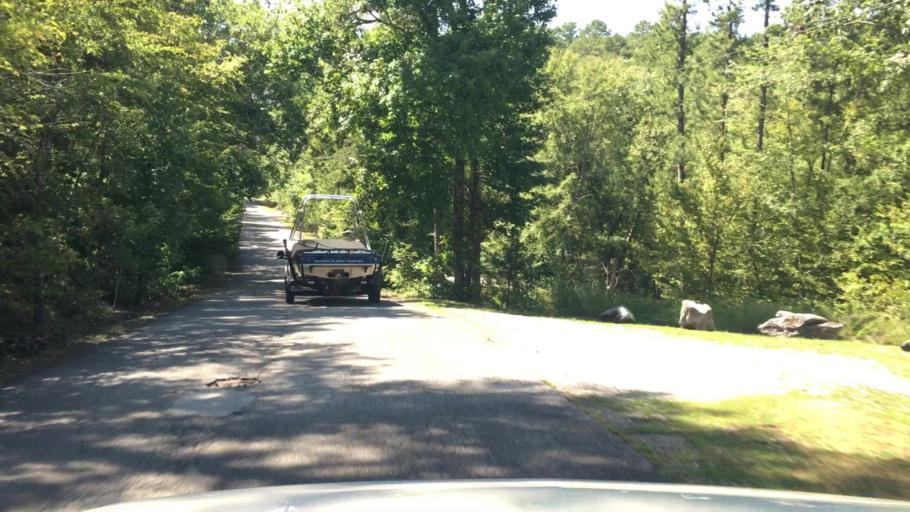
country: US
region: Arkansas
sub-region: Garland County
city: Piney
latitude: 34.5430
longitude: -93.3579
